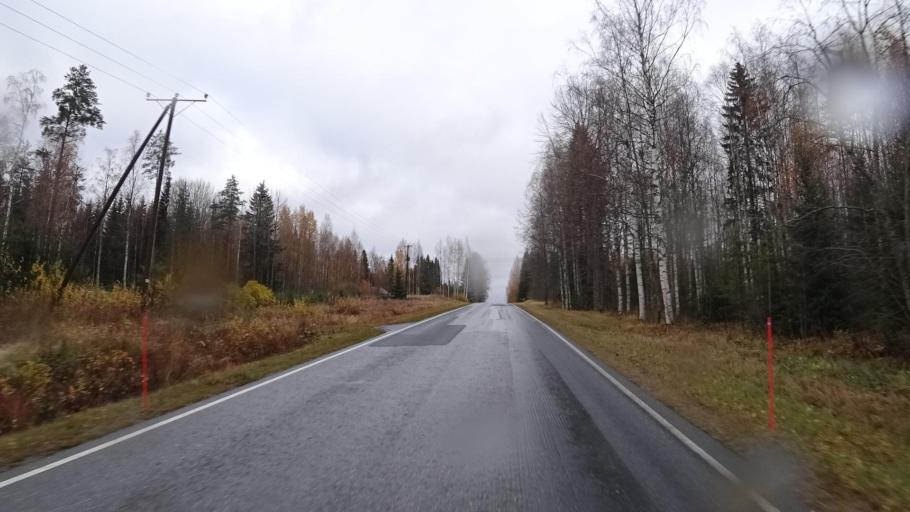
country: FI
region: North Karelia
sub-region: Joensuu
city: Polvijaervi
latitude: 63.0790
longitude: 29.5743
